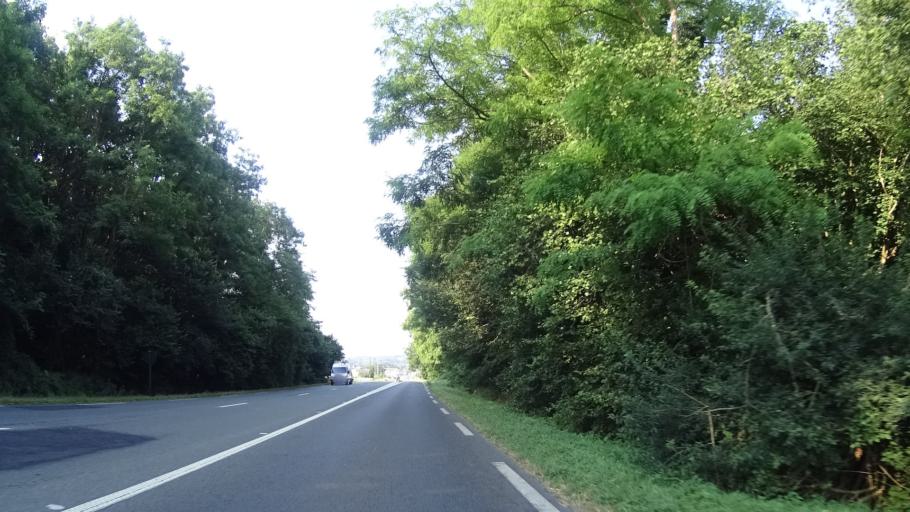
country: FR
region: Ile-de-France
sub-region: Departement du Val-d'Oise
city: Chaumontel
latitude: 49.1339
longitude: 2.4353
